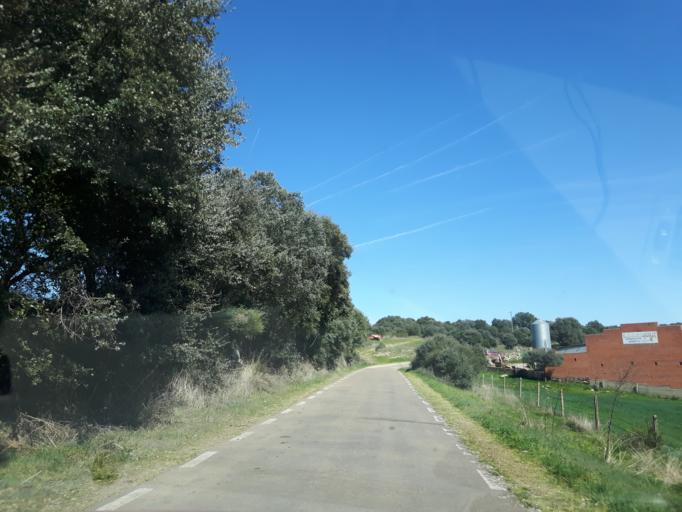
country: ES
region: Castille and Leon
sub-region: Provincia de Salamanca
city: Bermellar
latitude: 40.9986
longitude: -6.6602
